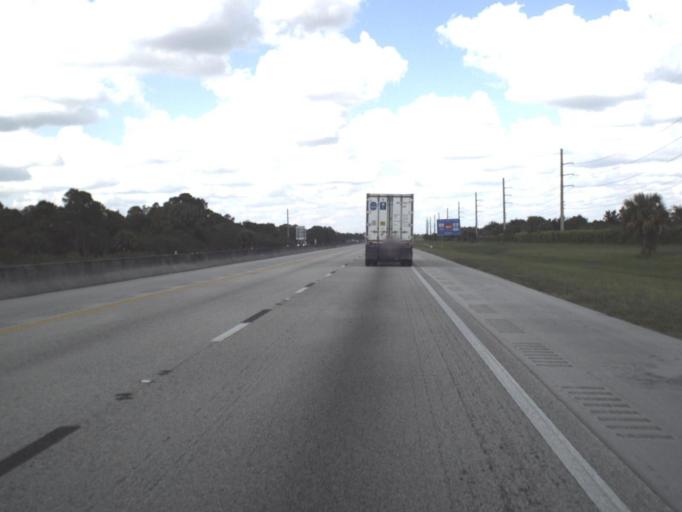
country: US
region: Florida
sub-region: Martin County
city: Palm City
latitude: 27.1824
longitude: -80.3188
